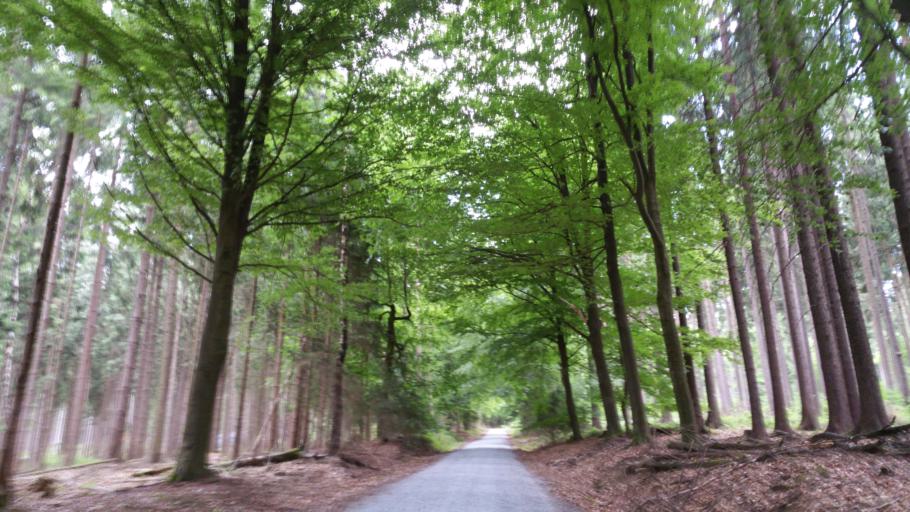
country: DE
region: Bavaria
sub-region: Upper Franconia
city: Kirchenlamitz
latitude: 50.1792
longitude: 11.9275
